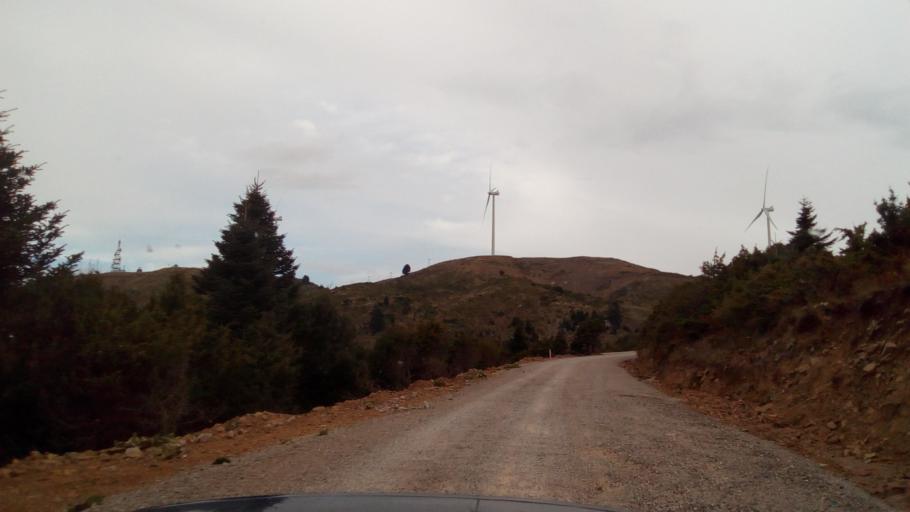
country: GR
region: Central Greece
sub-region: Nomos Fokidos
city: Lidoriki
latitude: 38.4499
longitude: 22.0739
